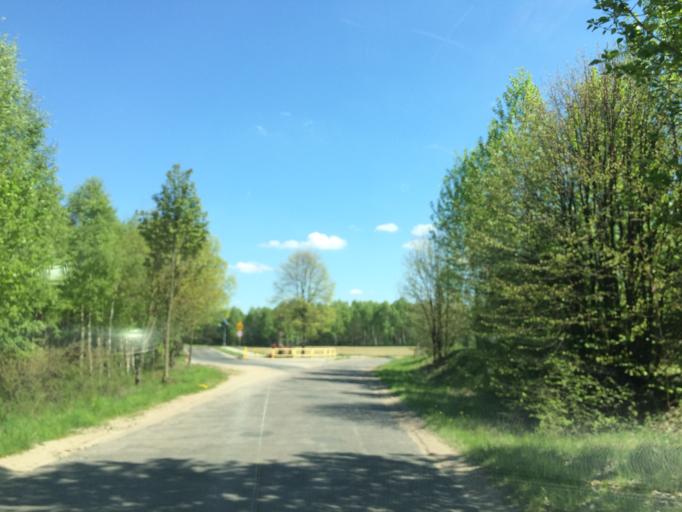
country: PL
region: Warmian-Masurian Voivodeship
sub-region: Powiat nowomiejski
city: Kurzetnik
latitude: 53.3848
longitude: 19.4767
